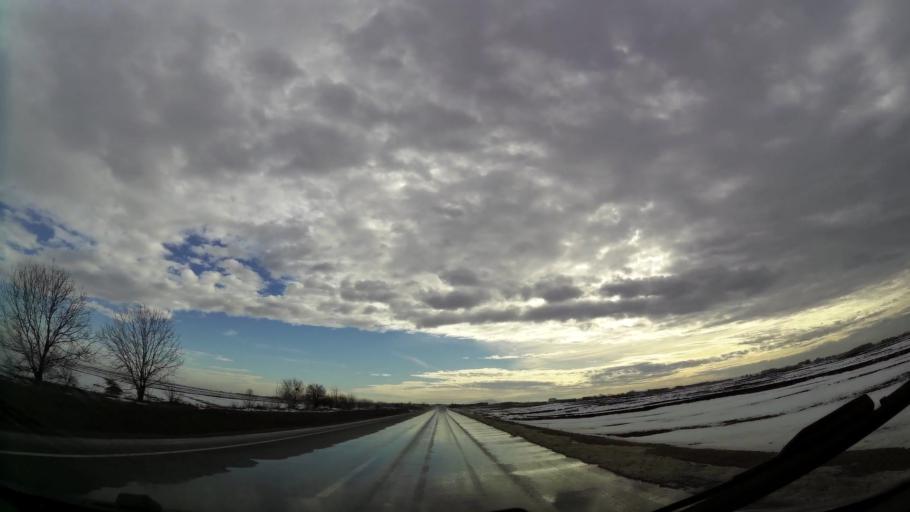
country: RS
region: Central Serbia
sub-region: Belgrade
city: Surcin
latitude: 44.8066
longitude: 20.3058
